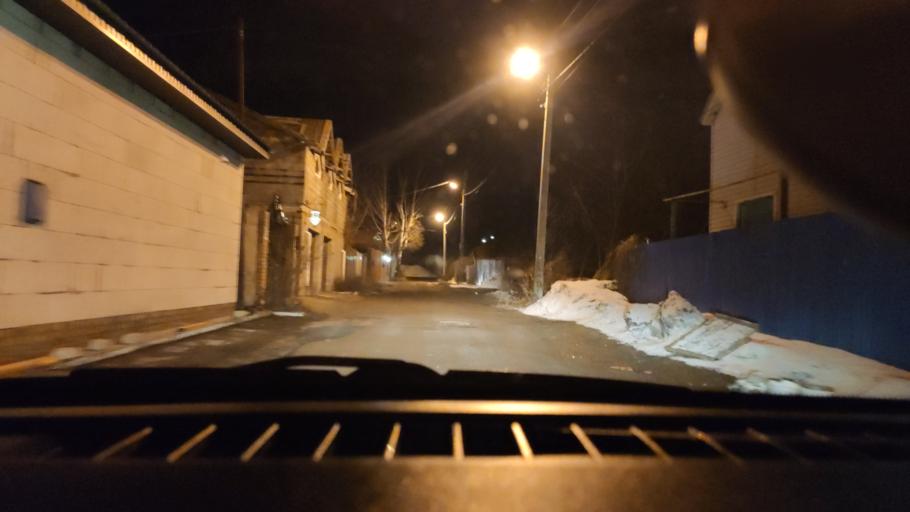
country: RU
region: Samara
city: Samara
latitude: 53.2680
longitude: 50.2322
